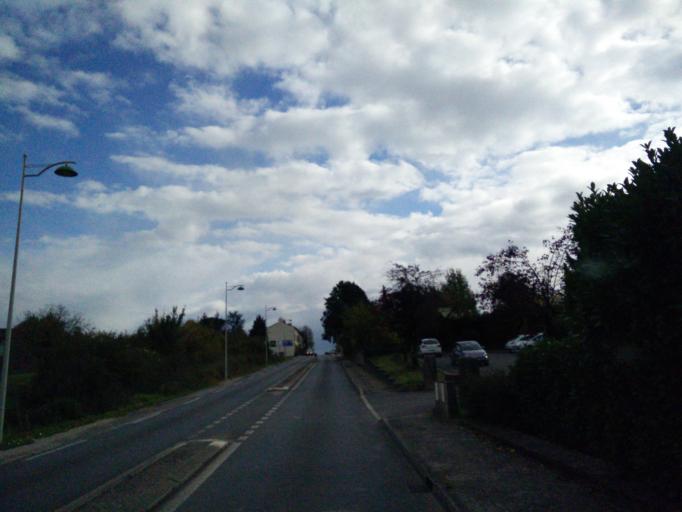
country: FR
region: Midi-Pyrenees
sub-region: Departement du Lot
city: Pradines
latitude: 44.4995
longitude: 1.3842
